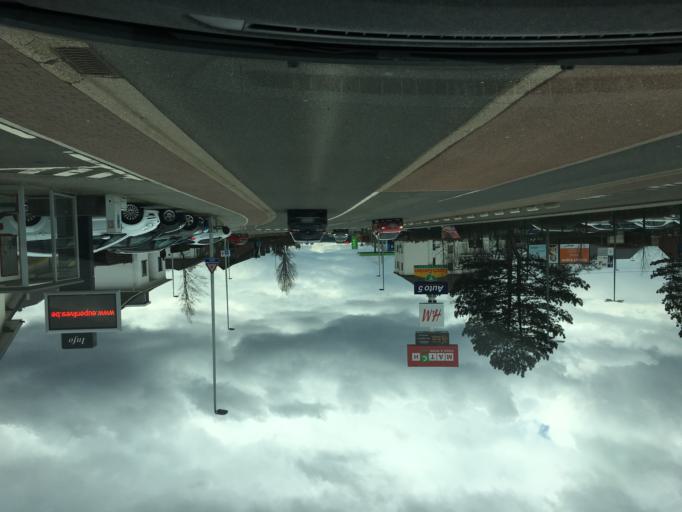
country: BE
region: Wallonia
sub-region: Province de Liege
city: Eupen
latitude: 50.6381
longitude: 6.0181
